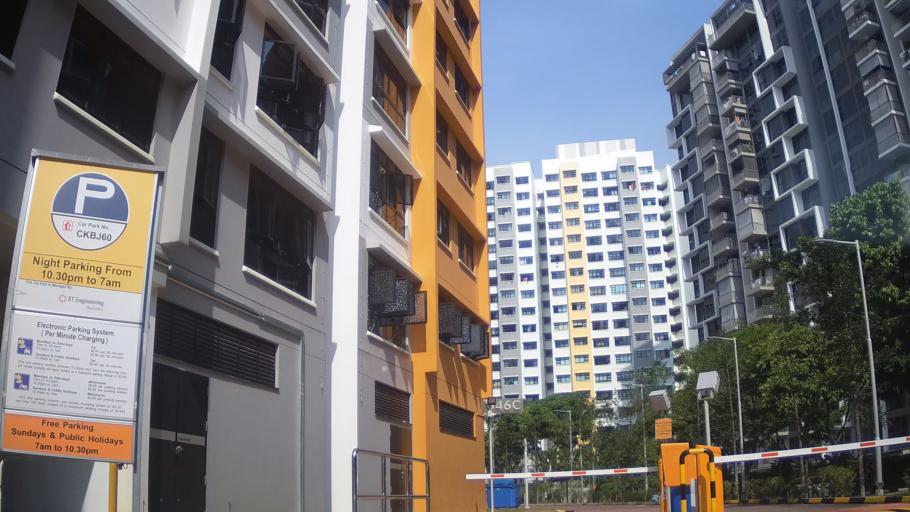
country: MY
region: Johor
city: Johor Bahru
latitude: 1.3891
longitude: 103.7699
